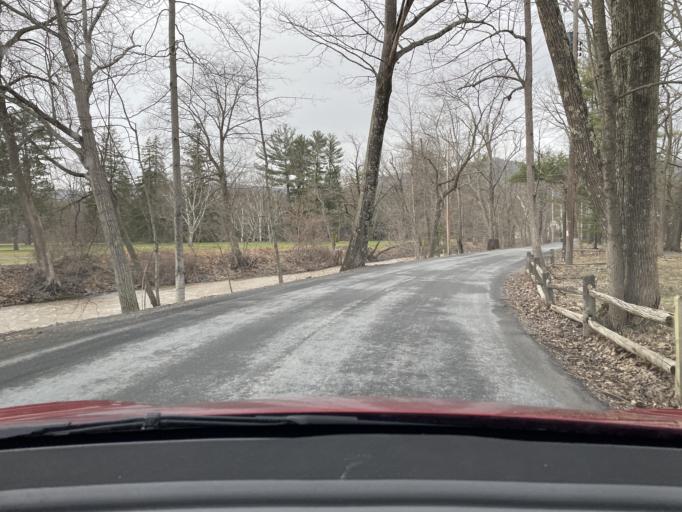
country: US
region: New York
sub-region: Ulster County
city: Woodstock
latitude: 42.0346
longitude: -74.1054
